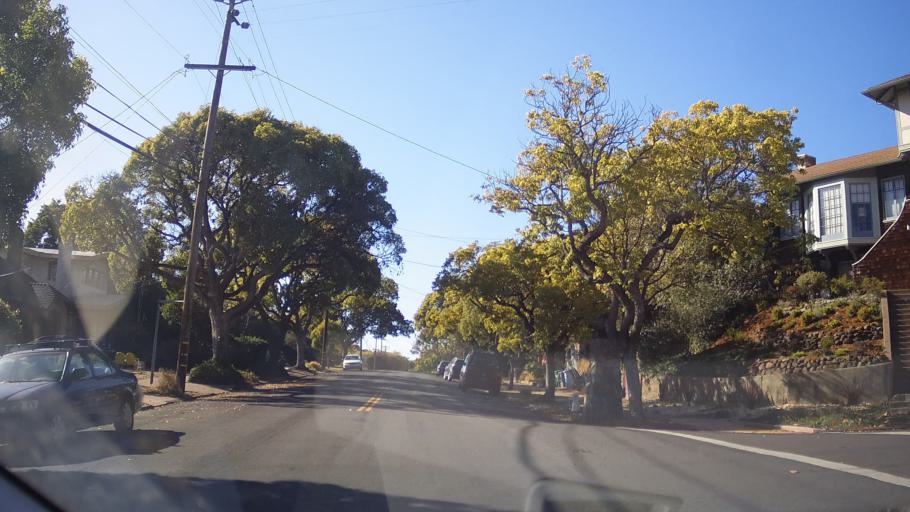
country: US
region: California
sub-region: Alameda County
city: Berkeley
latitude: 37.8855
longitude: -122.2770
